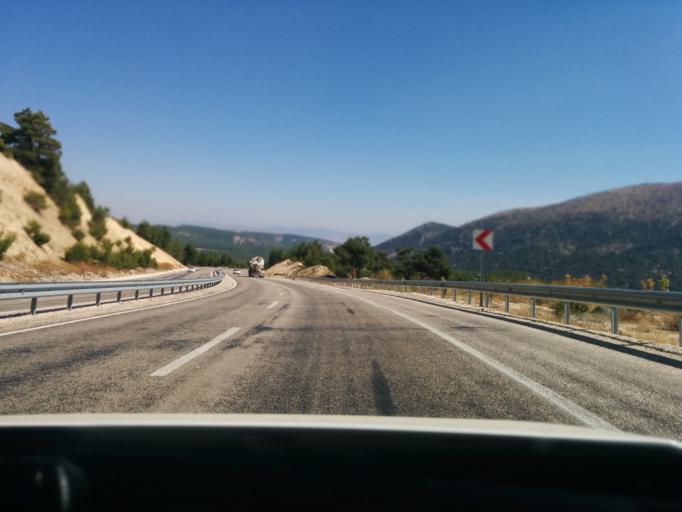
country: TR
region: Antalya
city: Korkuteli
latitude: 37.0378
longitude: 30.1027
